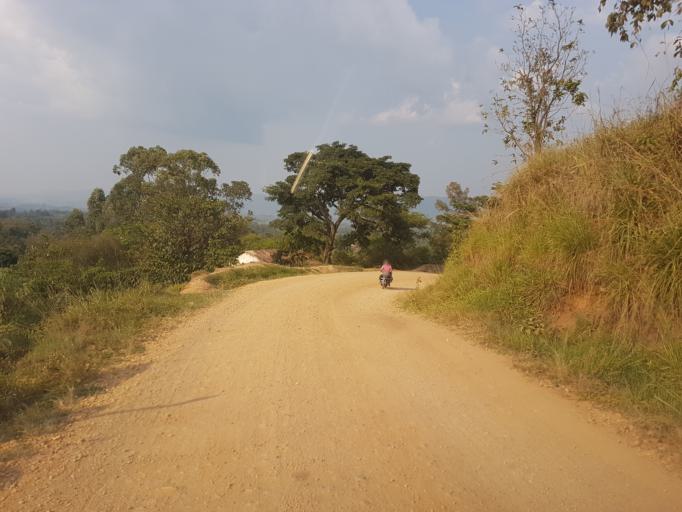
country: UG
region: Western Region
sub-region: Rukungiri District
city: Rukungiri
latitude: -0.6469
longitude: 29.8443
